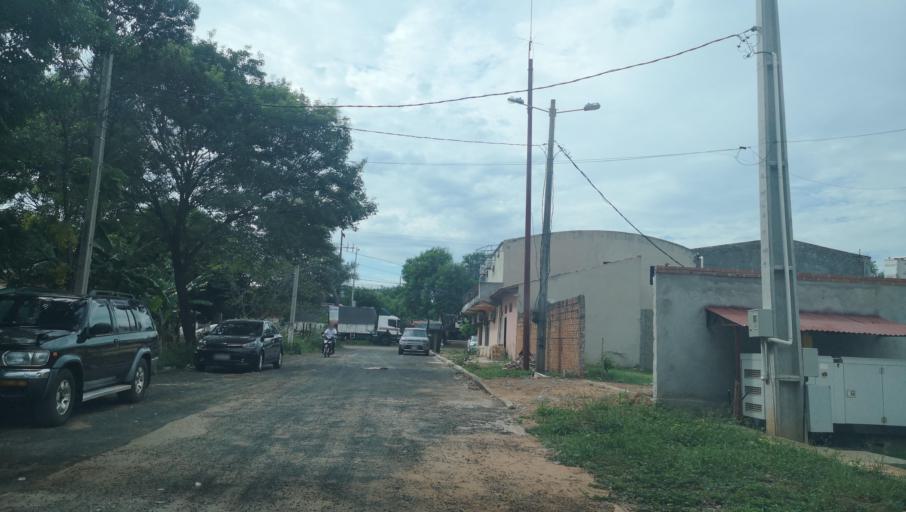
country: PY
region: San Pedro
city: Capiibary
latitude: -24.7299
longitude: -56.0207
